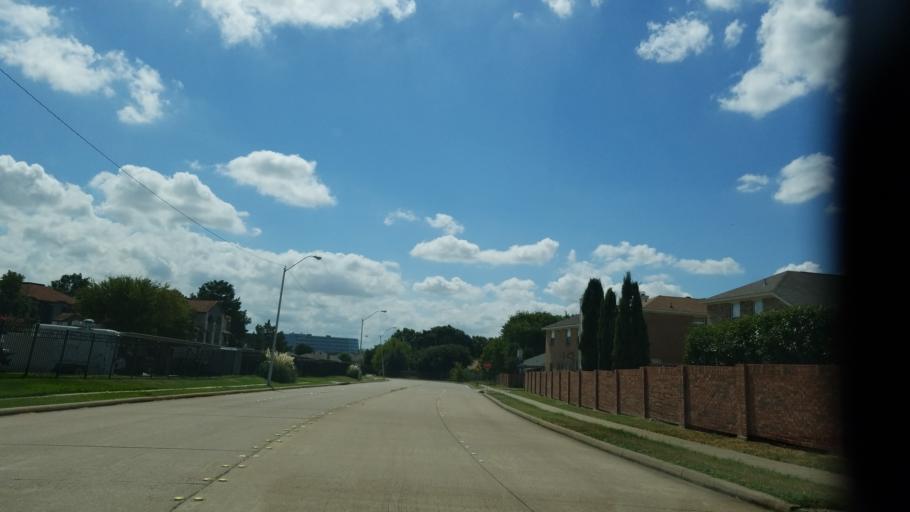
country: US
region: Texas
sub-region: Tarrant County
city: Euless
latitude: 32.8338
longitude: -97.0716
